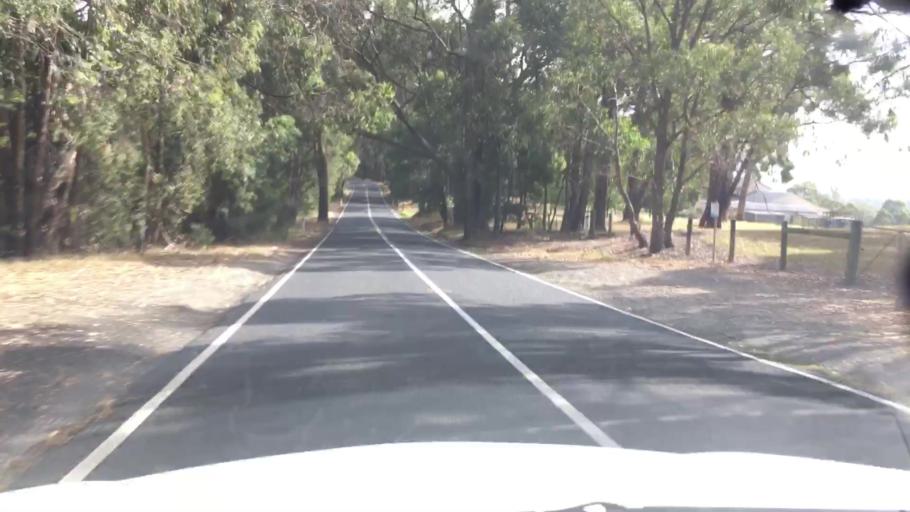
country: AU
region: Victoria
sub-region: Yarra Ranges
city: Macclesfield
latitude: -37.8428
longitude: 145.4861
